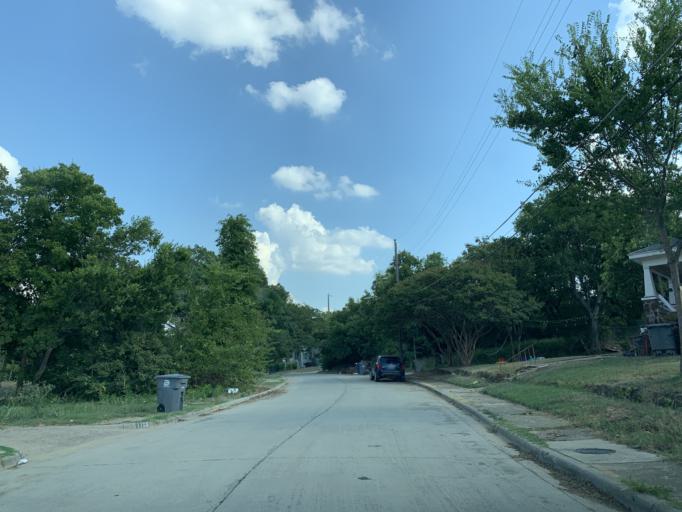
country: US
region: Texas
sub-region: Dallas County
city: Dallas
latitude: 32.7477
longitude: -96.8075
